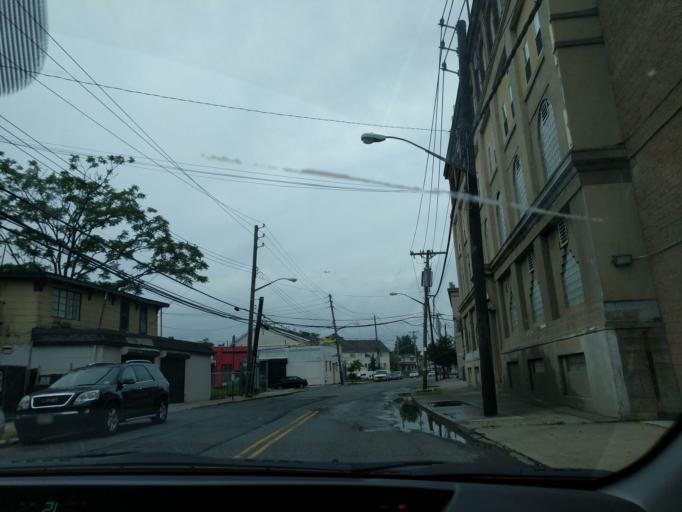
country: US
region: New York
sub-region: Richmond County
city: Bloomfield
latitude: 40.6378
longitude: -74.1616
